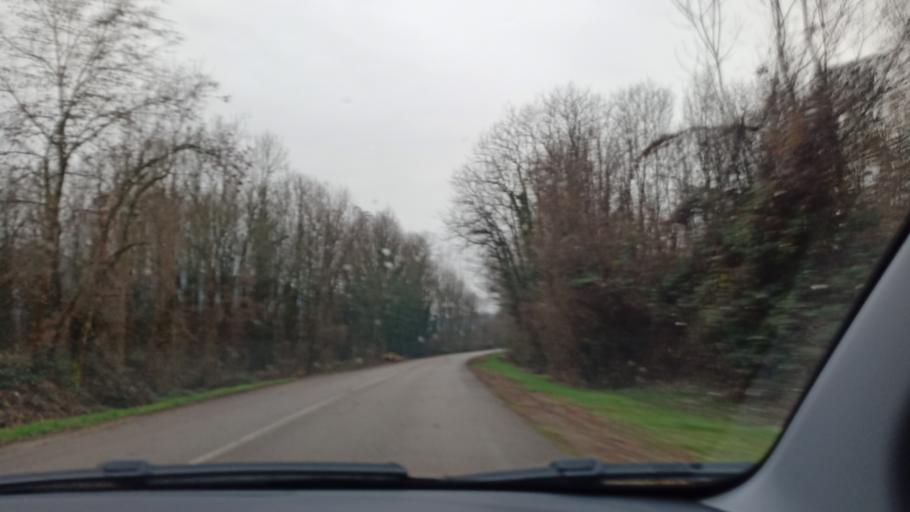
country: FR
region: Rhone-Alpes
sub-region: Departement de l'Isere
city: Domene
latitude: 45.2043
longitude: 5.8243
